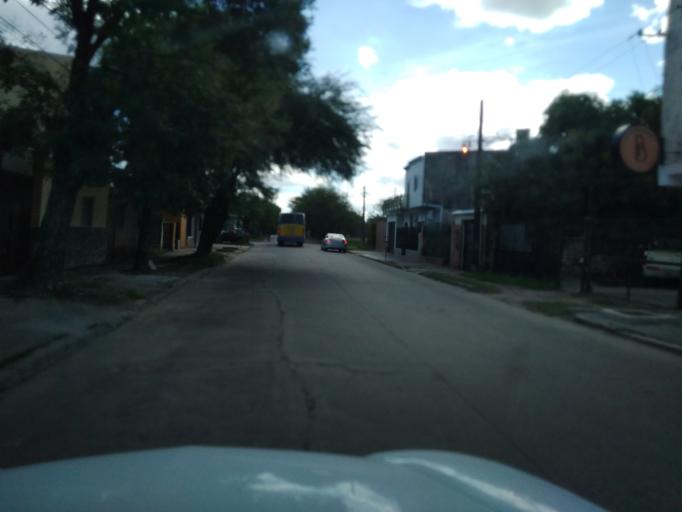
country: AR
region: Corrientes
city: Corrientes
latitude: -27.4957
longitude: -58.8365
